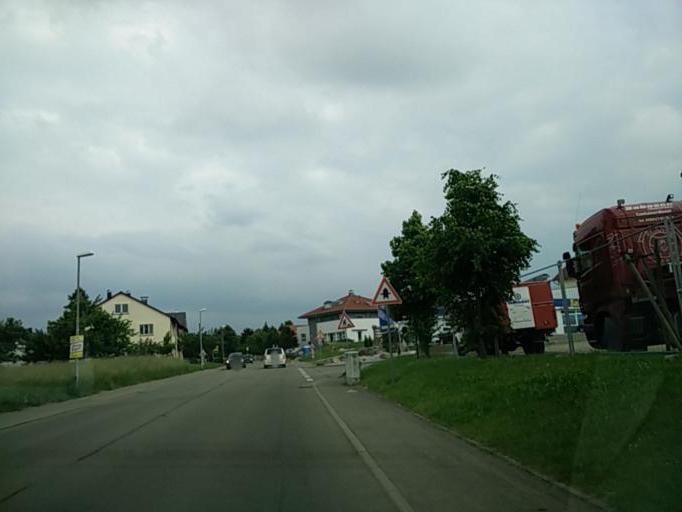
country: DE
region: Baden-Wuerttemberg
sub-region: Regierungsbezirk Stuttgart
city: Holzgerlingen
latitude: 48.6300
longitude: 9.0183
